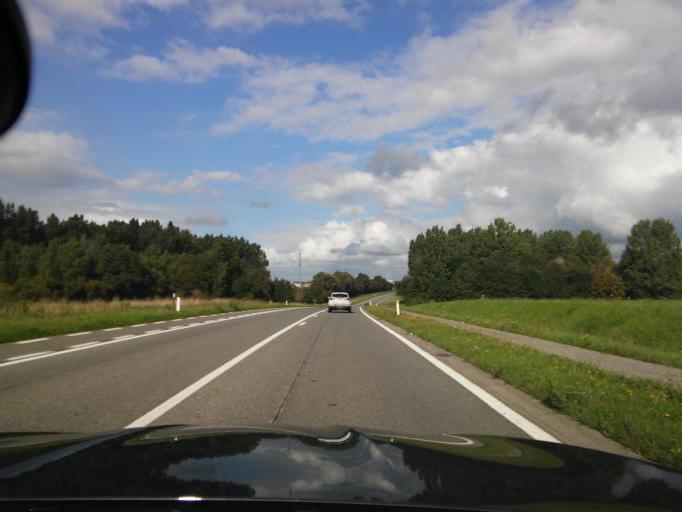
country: BE
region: Flanders
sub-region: Provincie Oost-Vlaanderen
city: Ninove
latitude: 50.8224
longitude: 3.9610
